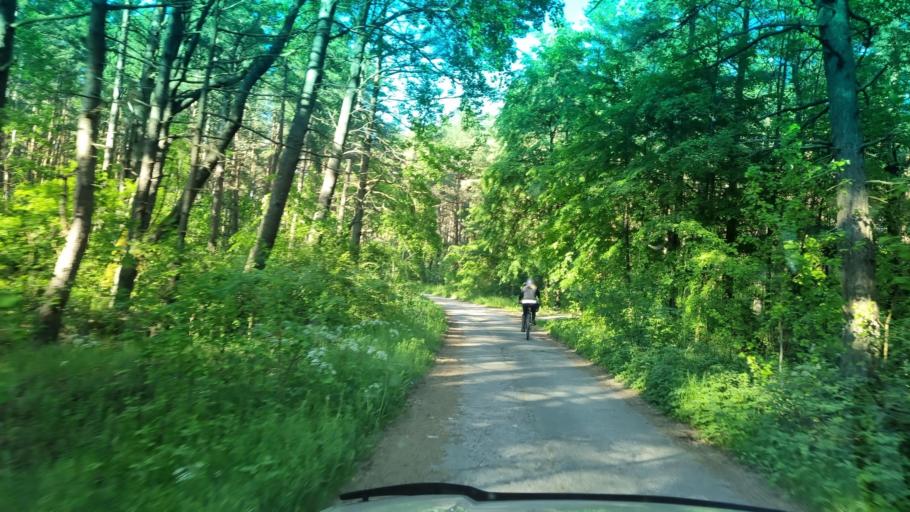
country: LV
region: Ventspils
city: Ventspils
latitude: 57.3728
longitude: 21.5241
